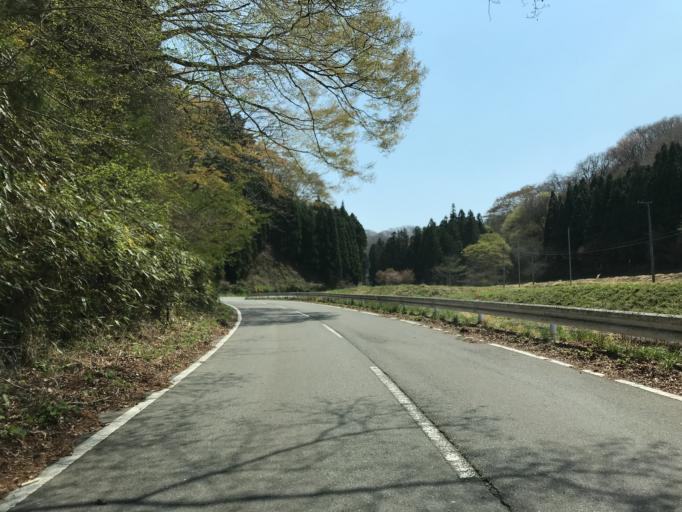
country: JP
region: Fukushima
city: Ishikawa
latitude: 36.9864
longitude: 140.6179
